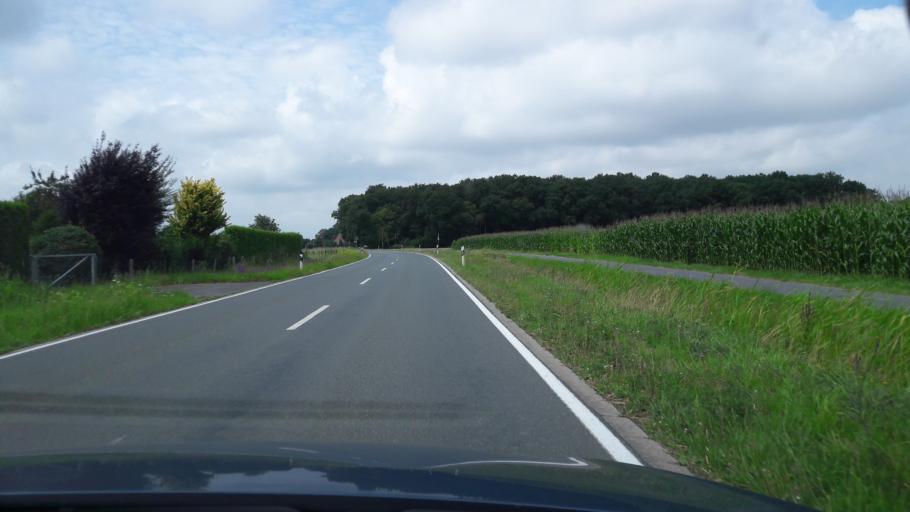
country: DE
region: North Rhine-Westphalia
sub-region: Regierungsbezirk Munster
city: Everswinkel
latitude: 51.9109
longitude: 7.8670
